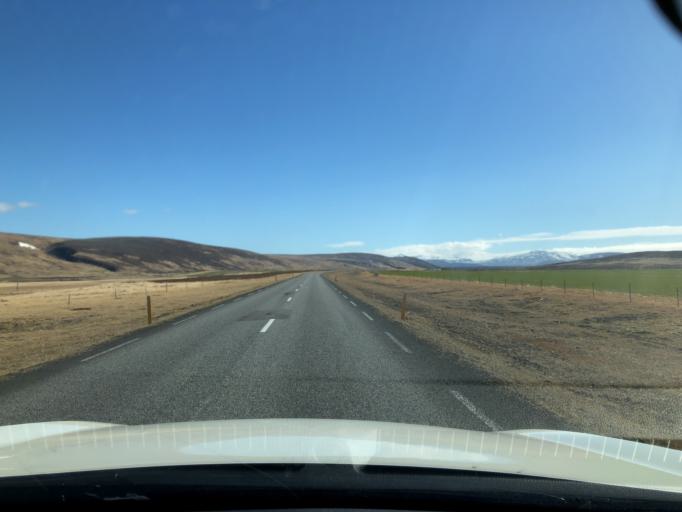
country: IS
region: South
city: Hveragerdi
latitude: 64.7001
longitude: -21.2223
